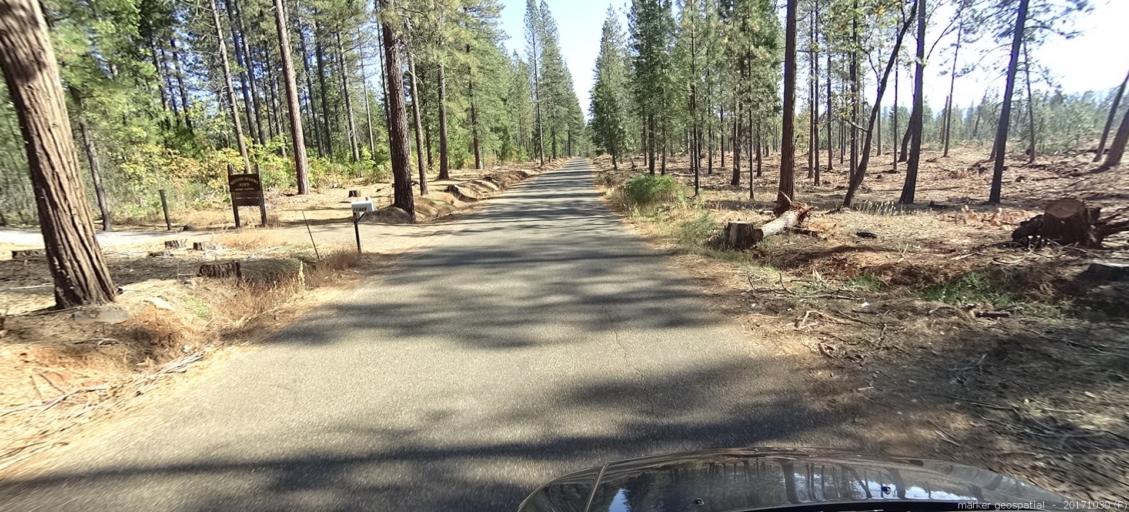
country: US
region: California
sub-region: Shasta County
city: Shingletown
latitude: 40.6103
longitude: -121.8717
